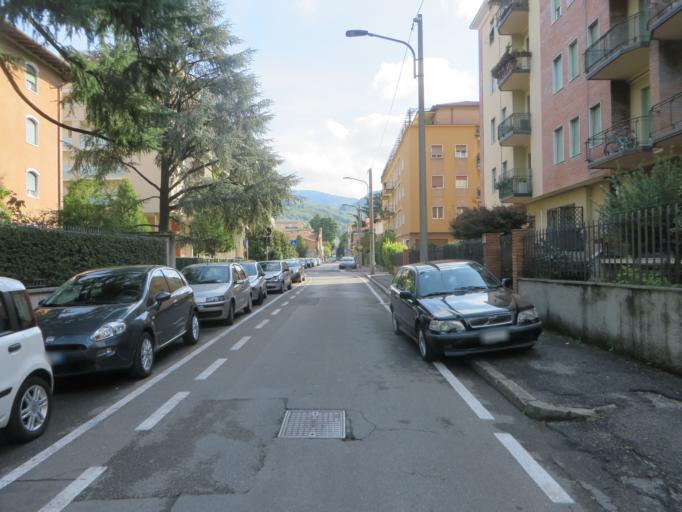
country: IT
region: Lombardy
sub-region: Provincia di Brescia
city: Brescia
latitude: 45.5517
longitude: 10.2192
